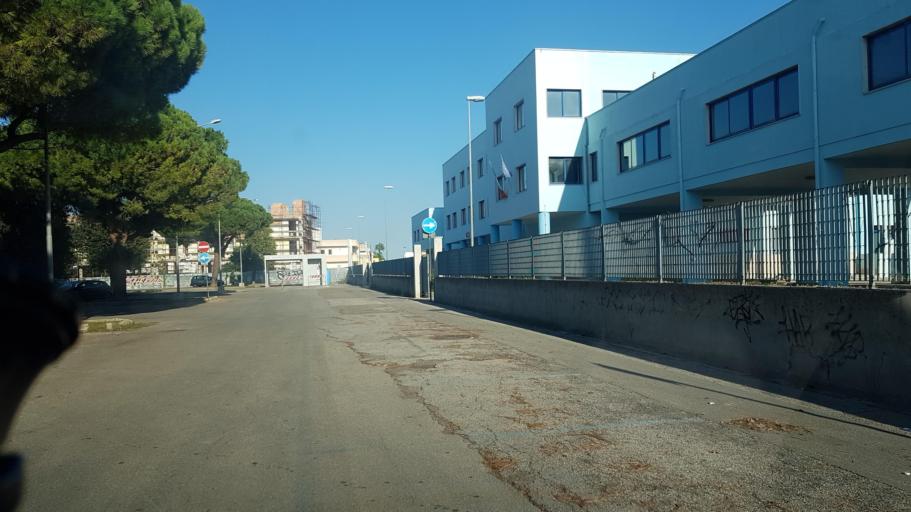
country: IT
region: Apulia
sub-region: Provincia di Brindisi
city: Mesagne
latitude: 40.5532
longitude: 17.8151
